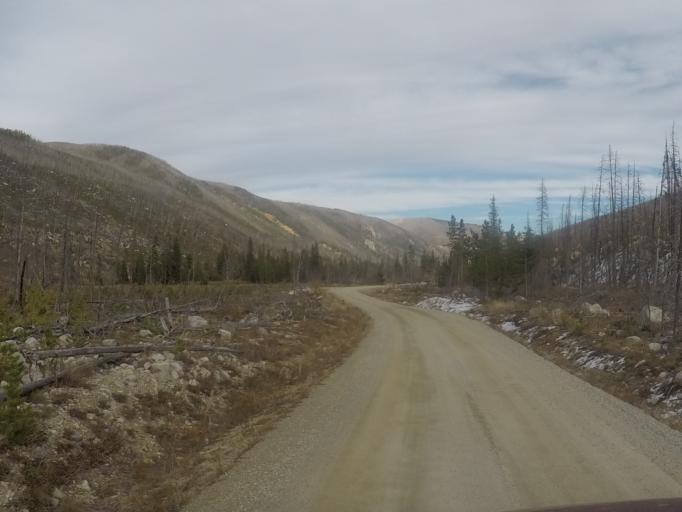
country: US
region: Montana
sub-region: Carbon County
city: Red Lodge
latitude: 45.1715
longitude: -109.4671
